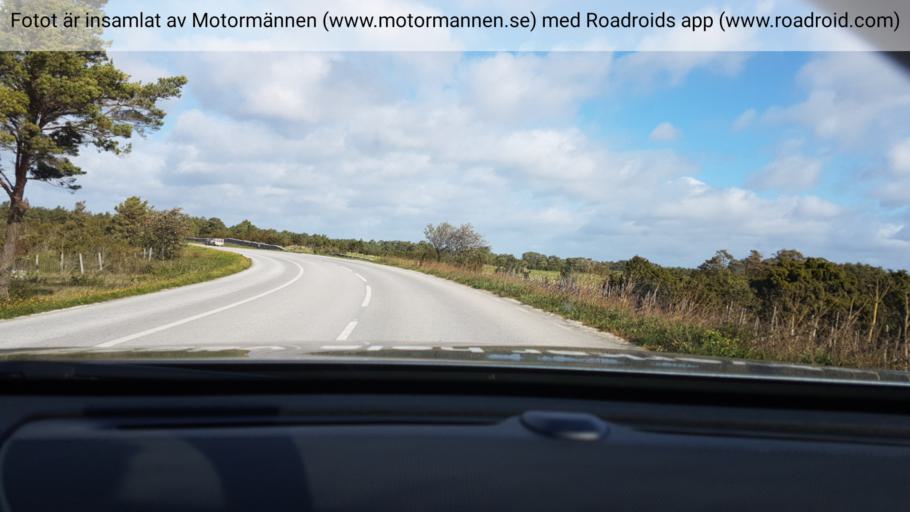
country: SE
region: Gotland
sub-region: Gotland
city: Slite
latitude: 57.8702
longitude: 19.0850
